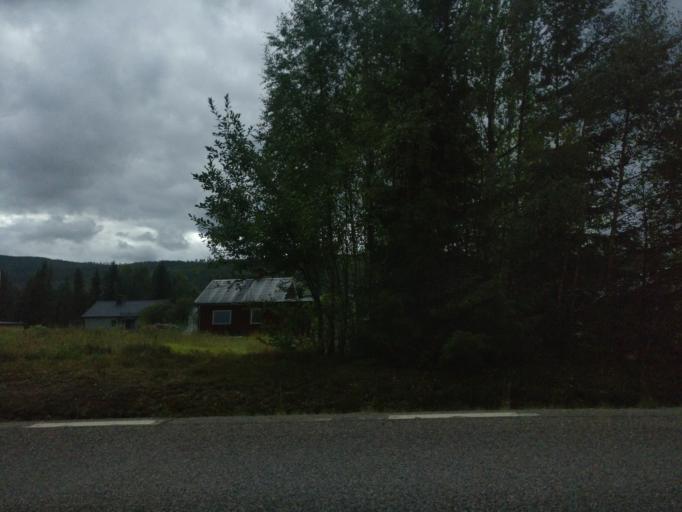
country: SE
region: Vaermland
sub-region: Torsby Kommun
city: Torsby
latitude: 60.7521
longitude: 12.7854
